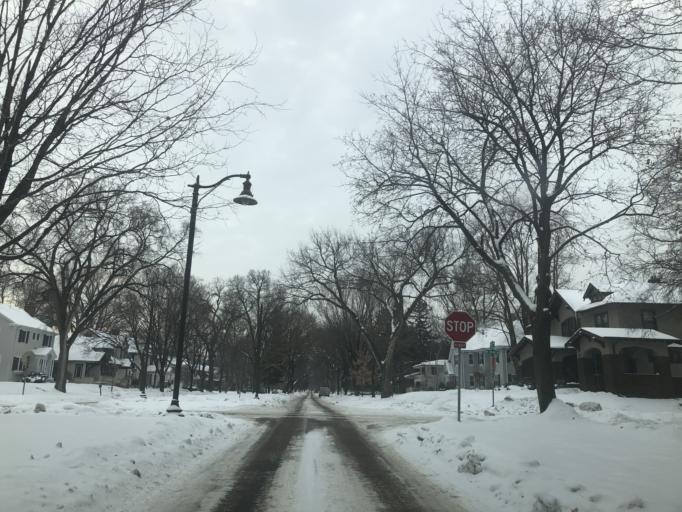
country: US
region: Minnesota
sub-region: Hennepin County
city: Richfield
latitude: 44.9253
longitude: -93.2936
